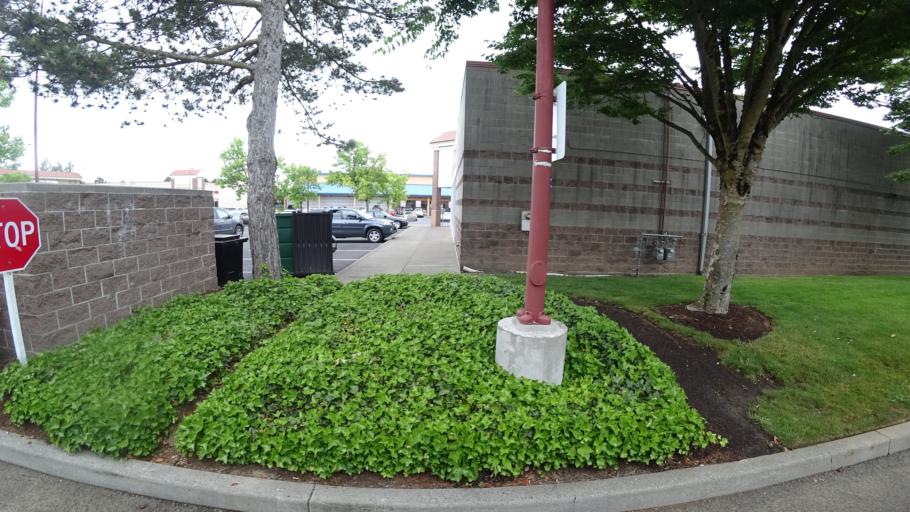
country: US
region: Oregon
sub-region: Washington County
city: Rockcreek
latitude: 45.5370
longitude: -122.8682
